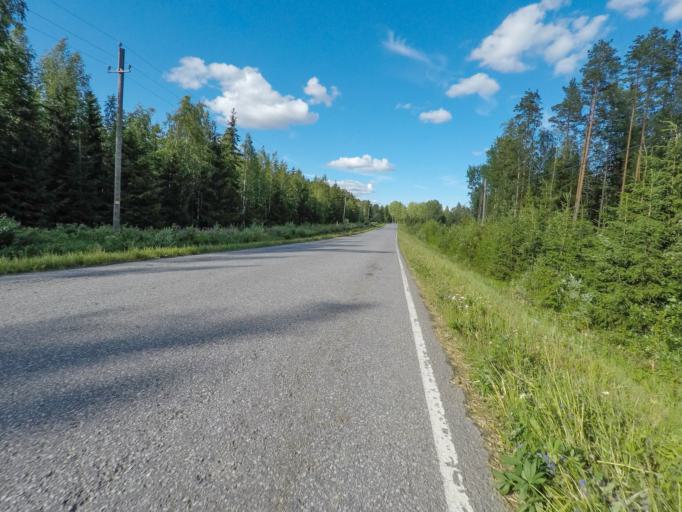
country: FI
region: South Karelia
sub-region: Imatra
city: Imatra
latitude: 61.1390
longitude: 28.7392
